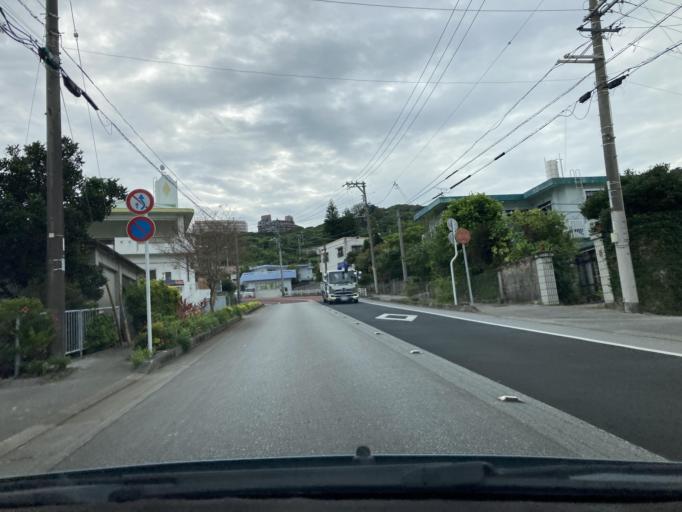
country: JP
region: Okinawa
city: Tomigusuku
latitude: 26.1704
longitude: 127.7722
